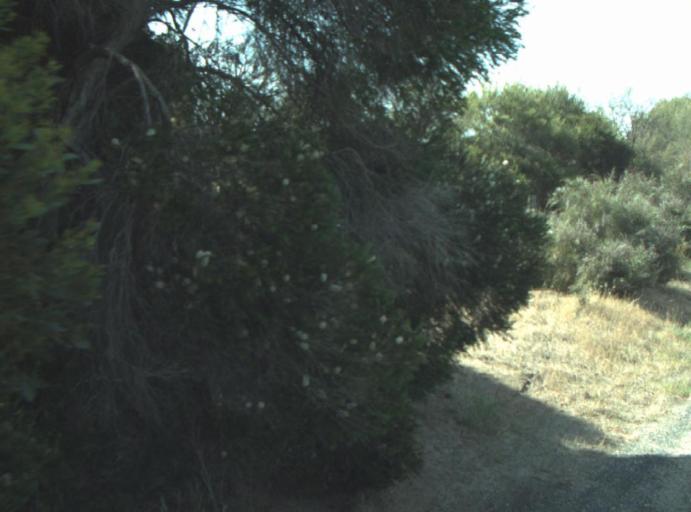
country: AU
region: Victoria
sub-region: Greater Geelong
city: Leopold
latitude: -38.1800
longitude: 144.5131
